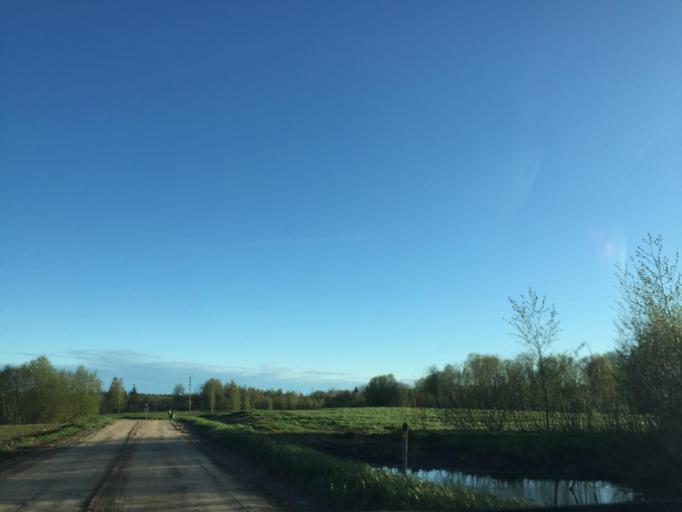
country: LV
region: Vecpiebalga
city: Vecpiebalga
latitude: 56.8434
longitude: 25.9564
